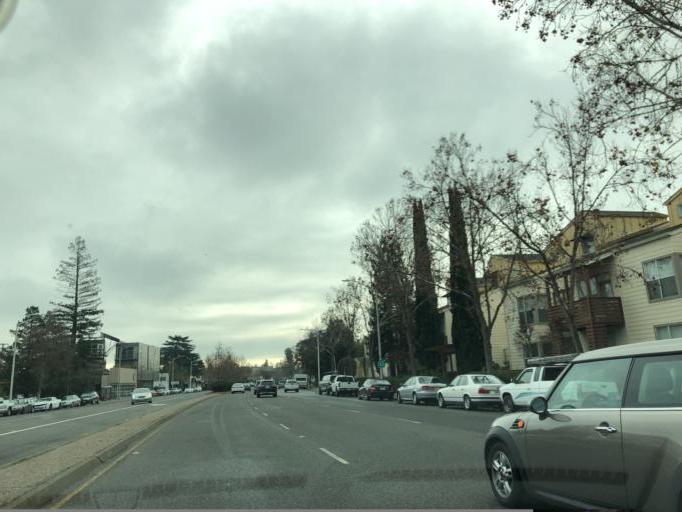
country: US
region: California
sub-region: Santa Clara County
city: Palo Alto
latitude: 37.4157
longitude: -122.1282
